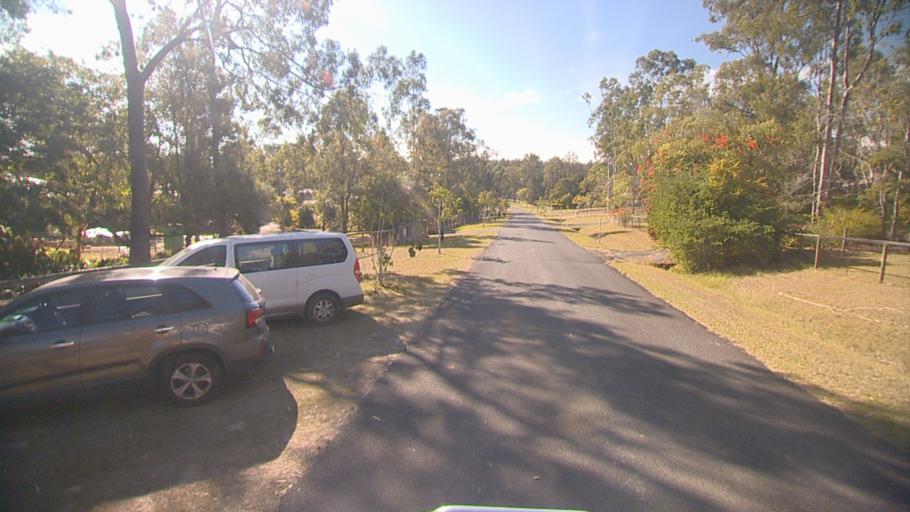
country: AU
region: Queensland
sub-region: Ipswich
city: Springfield Lakes
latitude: -27.7337
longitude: 152.9286
